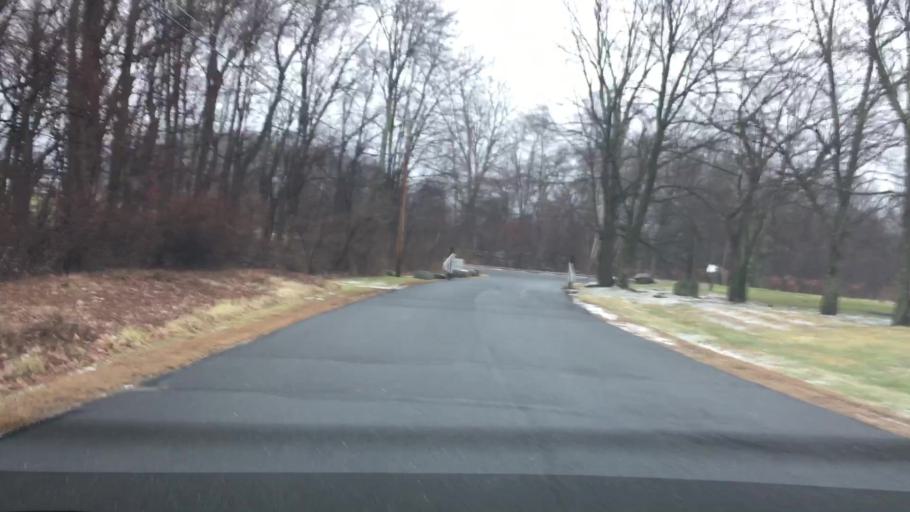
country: US
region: Connecticut
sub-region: Litchfield County
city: Oakville
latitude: 41.6134
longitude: -73.0902
